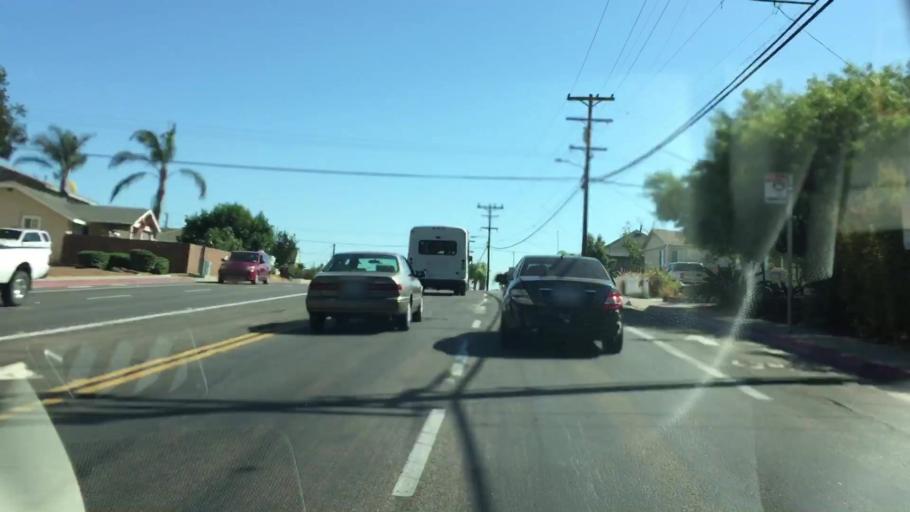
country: US
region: California
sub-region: San Diego County
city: La Mesa
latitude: 32.7707
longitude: -117.0472
